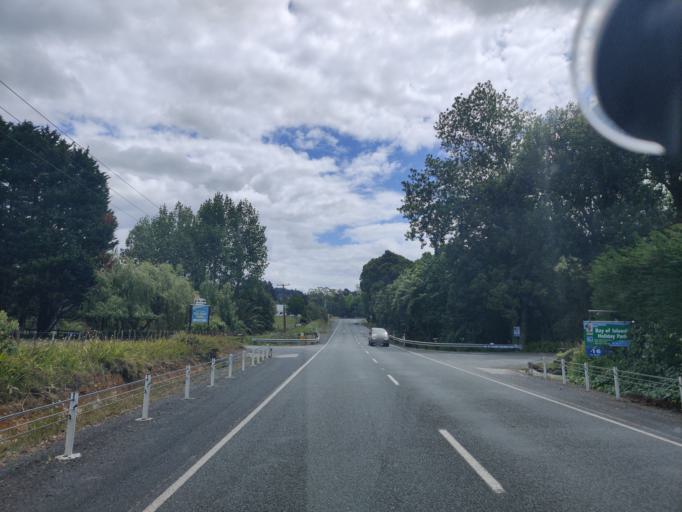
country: NZ
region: Northland
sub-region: Far North District
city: Paihia
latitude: -35.2906
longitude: 174.0189
